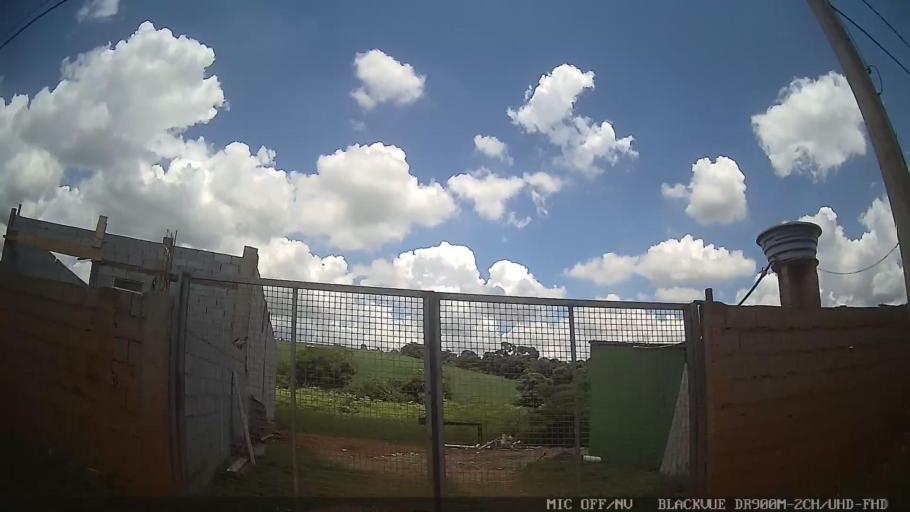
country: BR
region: Sao Paulo
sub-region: Atibaia
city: Atibaia
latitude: -23.1148
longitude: -46.6215
